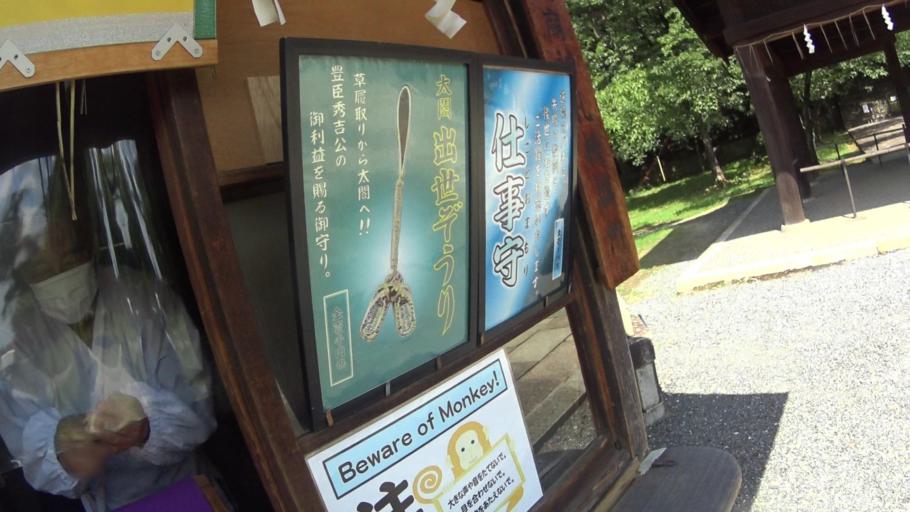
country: RU
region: Rostov
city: Remontnoye
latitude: 46.4994
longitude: 43.7742
